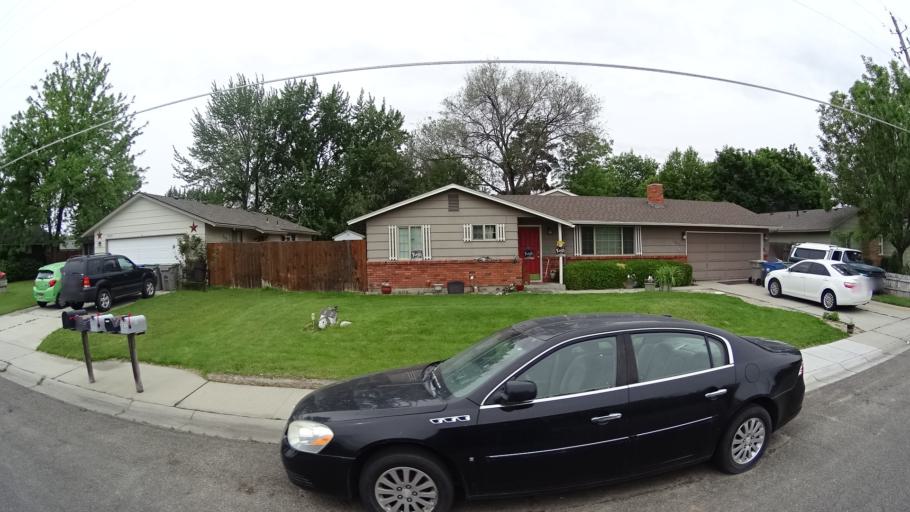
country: US
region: Idaho
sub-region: Ada County
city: Garden City
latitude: 43.6347
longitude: -116.3068
